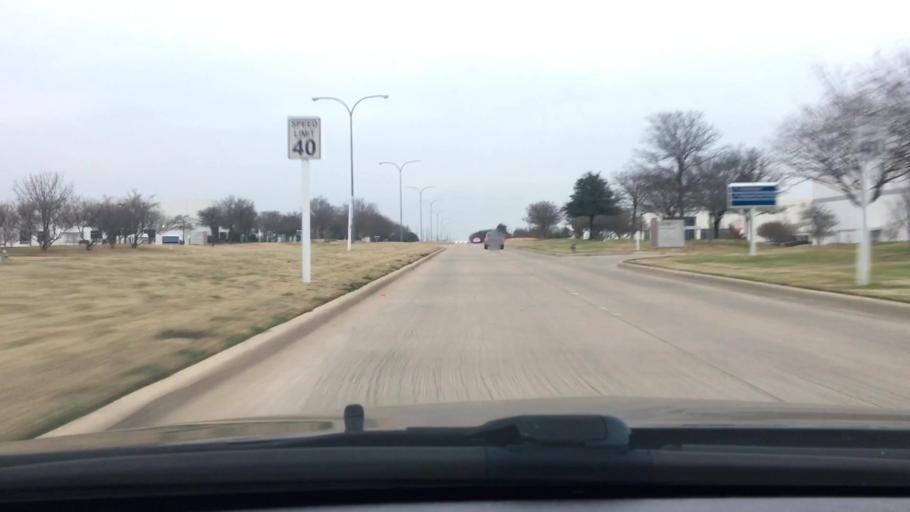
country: US
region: Texas
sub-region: Tarrant County
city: Keller
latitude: 32.9729
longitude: -97.2628
